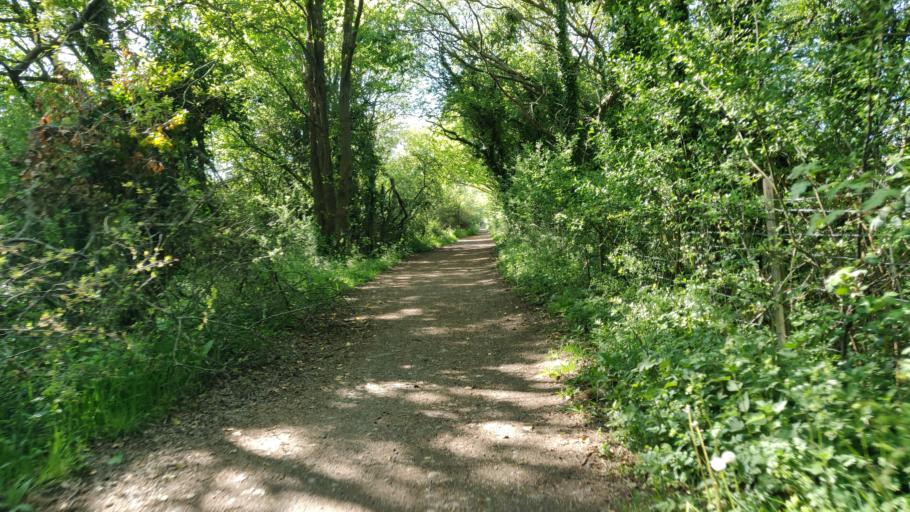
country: GB
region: England
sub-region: West Sussex
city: Rudgwick
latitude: 51.0638
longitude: -0.3987
